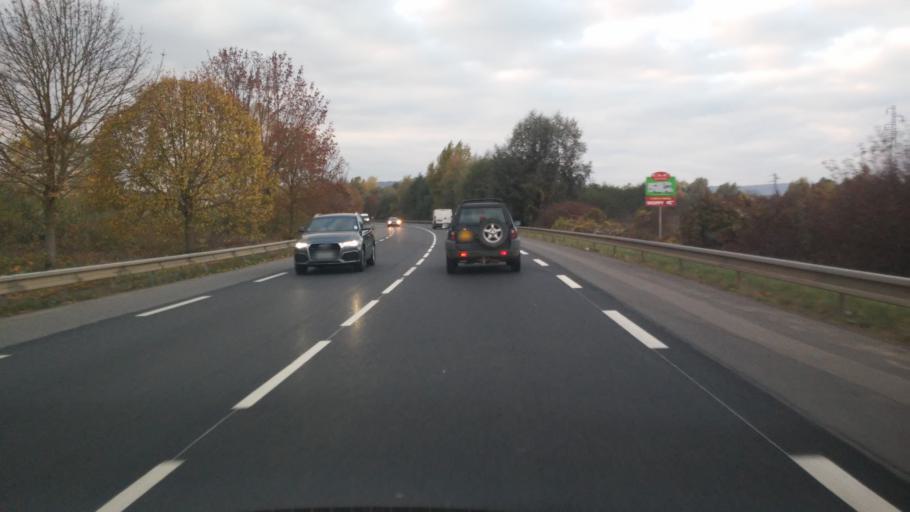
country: FR
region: Lorraine
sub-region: Departement de la Moselle
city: Woippy
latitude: 49.1567
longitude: 6.1647
